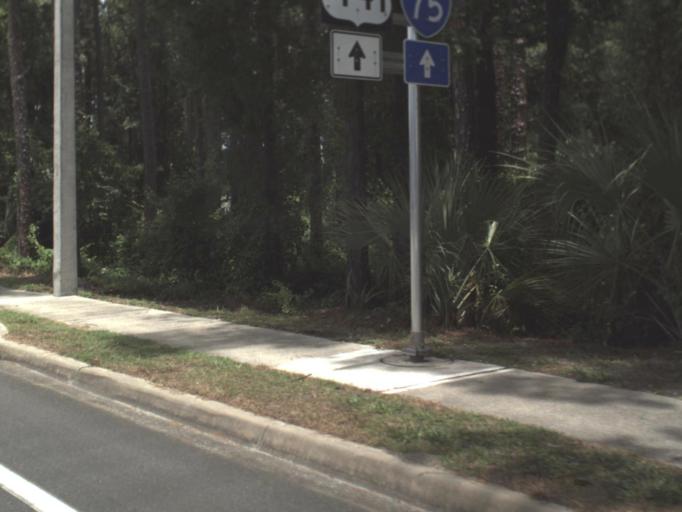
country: US
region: Florida
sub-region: Alachua County
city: Gainesville
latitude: 29.6845
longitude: -82.2880
